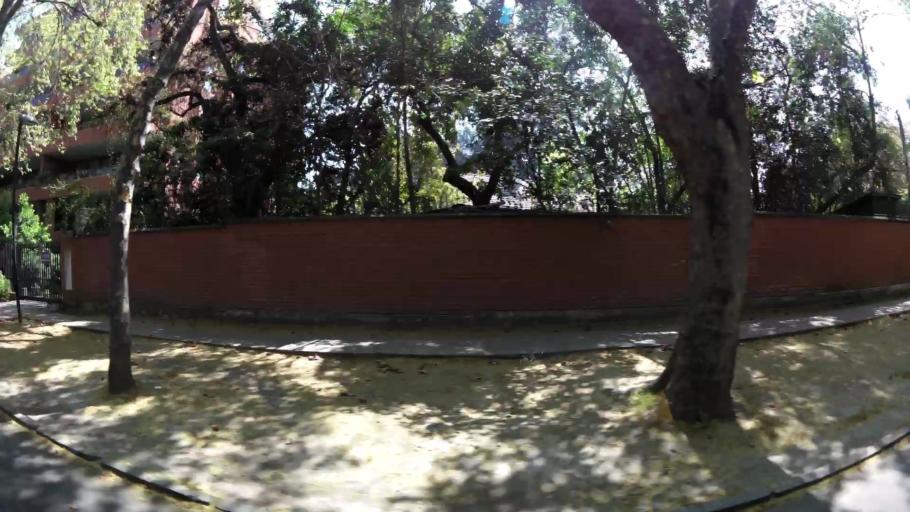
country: CL
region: Santiago Metropolitan
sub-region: Provincia de Santiago
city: Villa Presidente Frei, Nunoa, Santiago, Chile
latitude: -33.3950
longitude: -70.5912
